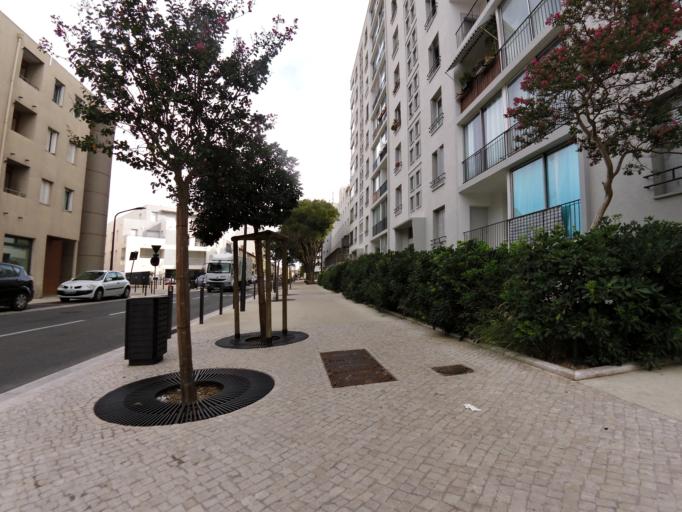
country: FR
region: Languedoc-Roussillon
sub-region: Departement du Gard
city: Nimes
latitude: 43.8273
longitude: 4.3541
